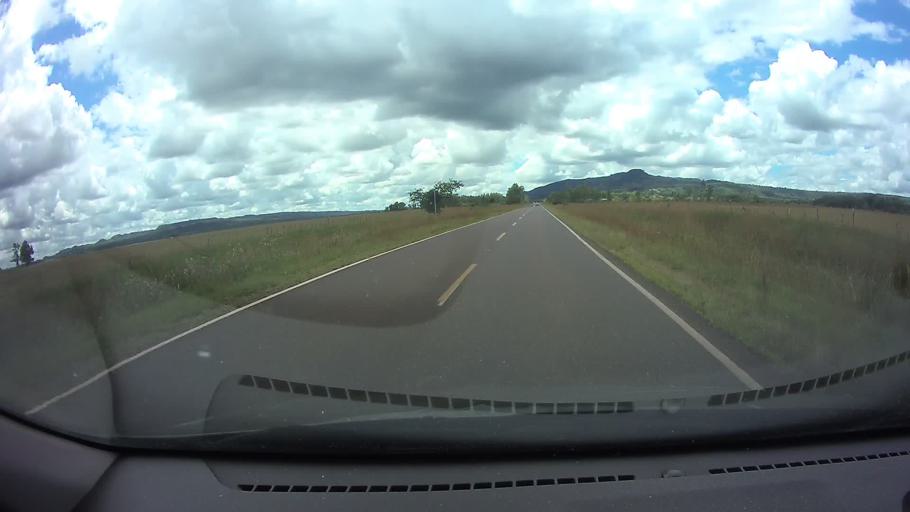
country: PY
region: Paraguari
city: Ybycui
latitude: -25.9097
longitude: -57.0133
